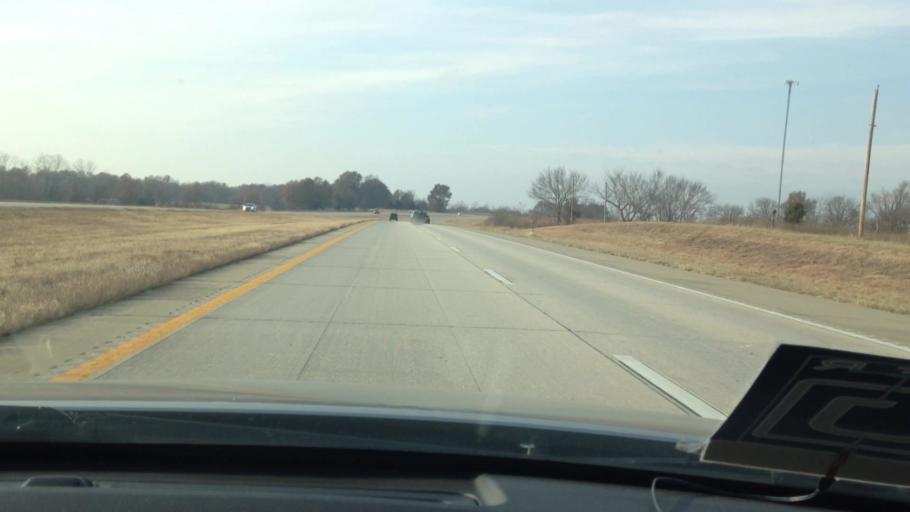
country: US
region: Missouri
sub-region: Henry County
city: Clinton
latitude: 38.4407
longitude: -93.9488
